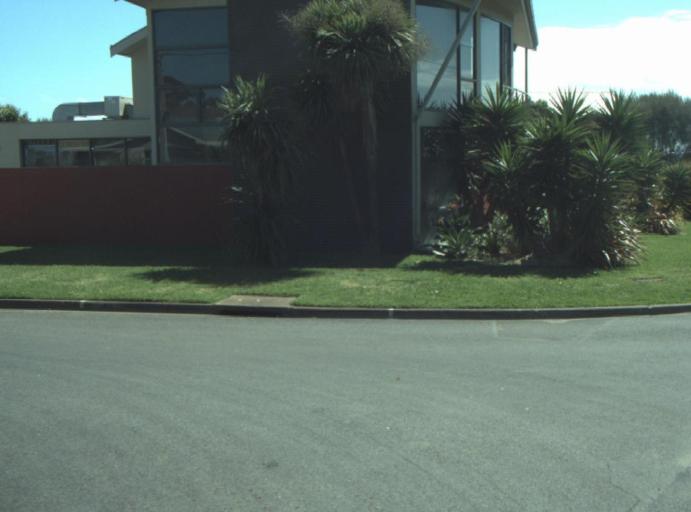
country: AU
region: Victoria
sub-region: Queenscliffe
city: Queenscliff
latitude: -38.1851
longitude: 144.7134
